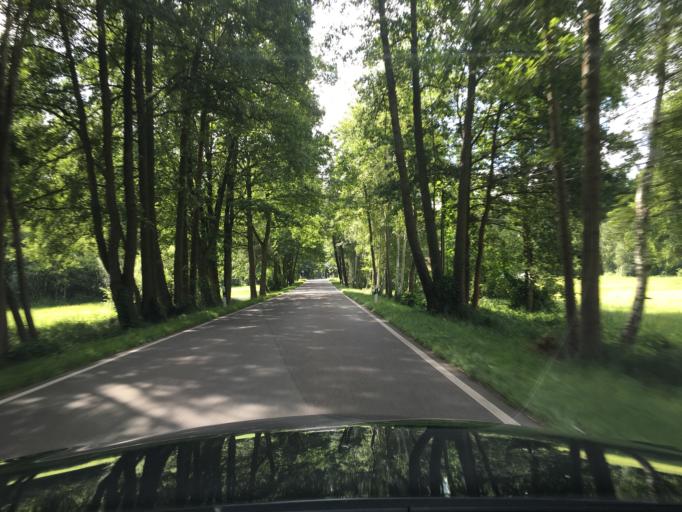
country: DE
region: Brandenburg
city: Burg
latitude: 51.8397
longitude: 14.1074
